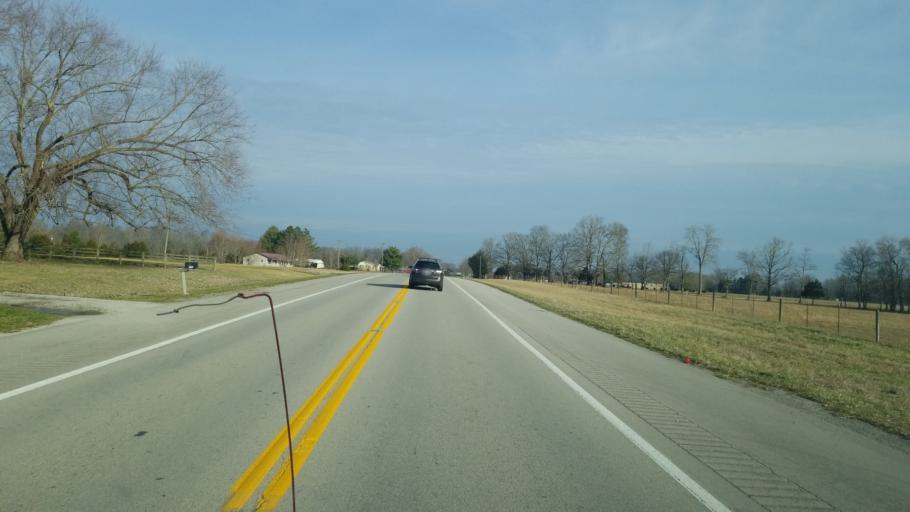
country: US
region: Kentucky
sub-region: Russell County
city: Russell Springs
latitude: 37.1328
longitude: -85.0343
